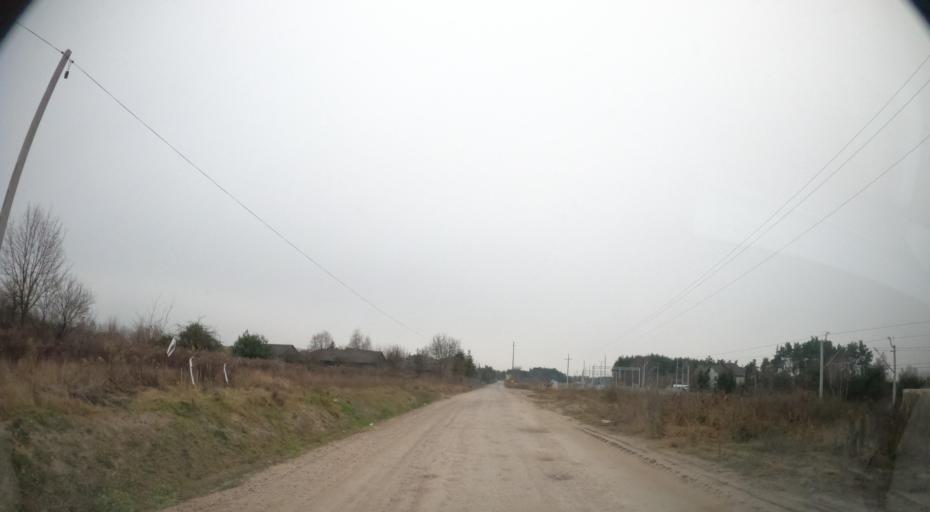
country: PL
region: Masovian Voivodeship
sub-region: Powiat radomski
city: Jastrzebia
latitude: 51.4813
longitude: 21.1937
